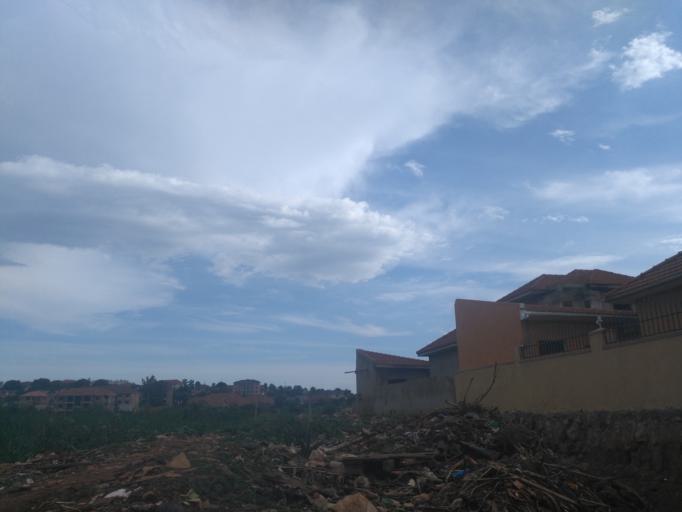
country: UG
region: Central Region
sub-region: Wakiso District
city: Kireka
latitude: 0.3791
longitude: 32.6194
